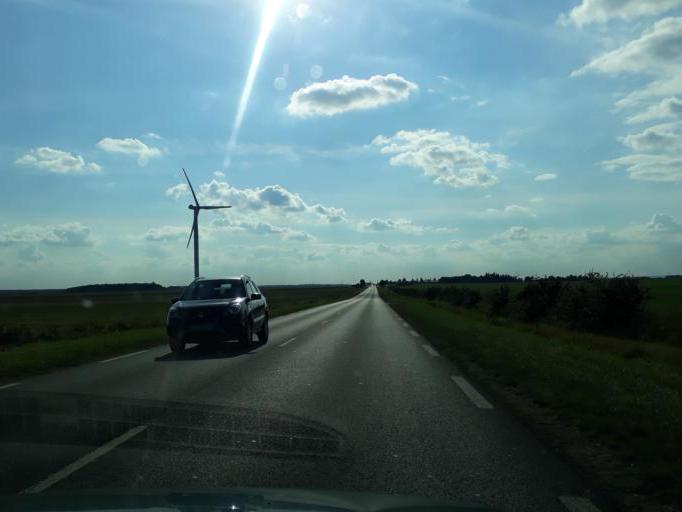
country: FR
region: Centre
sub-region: Departement du Loir-et-Cher
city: Ouzouer-le-Marche
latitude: 47.9042
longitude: 1.4556
